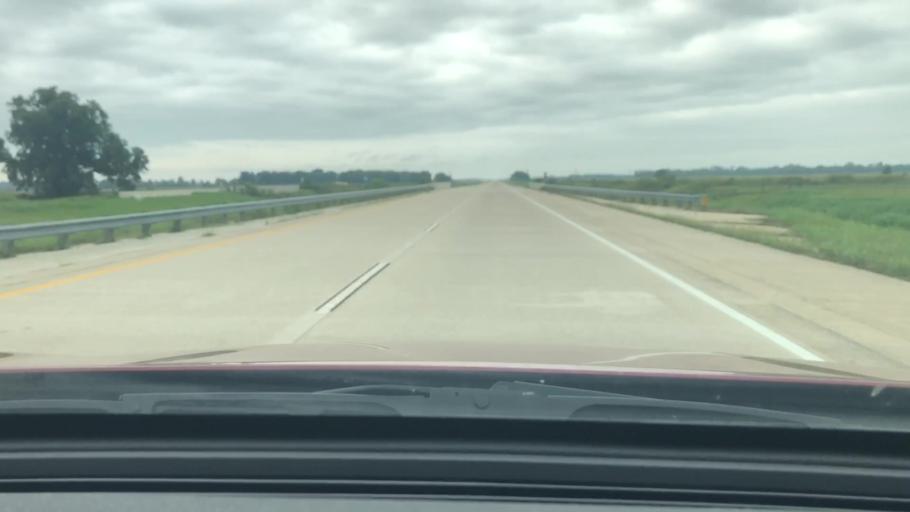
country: US
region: Louisiana
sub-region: Caddo Parish
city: Oil City
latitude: 32.7319
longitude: -93.8742
